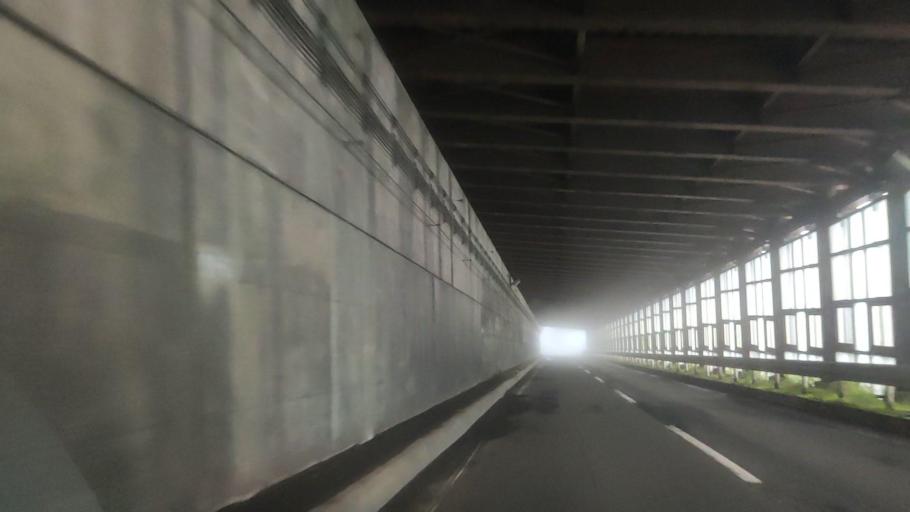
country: JP
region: Hokkaido
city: Date
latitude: 42.5513
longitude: 141.0820
